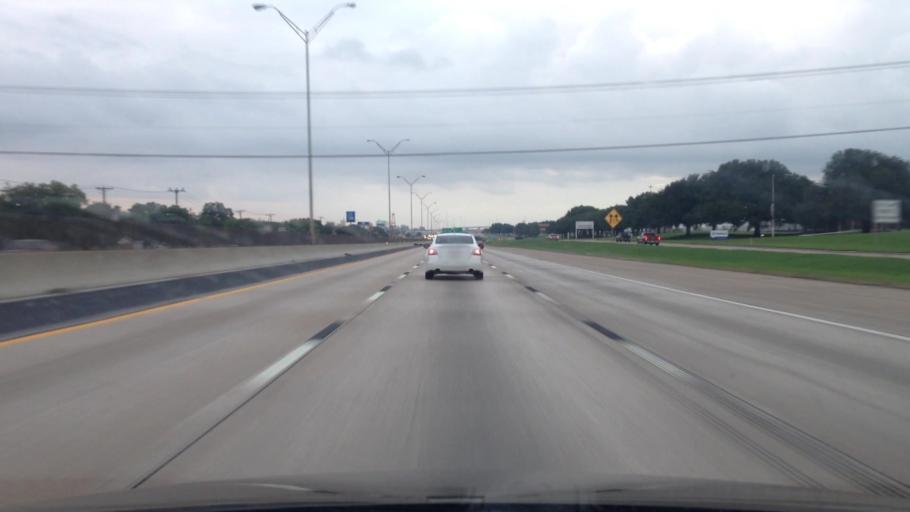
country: US
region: Texas
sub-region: Tarrant County
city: Edgecliff Village
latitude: 32.6453
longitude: -97.3225
